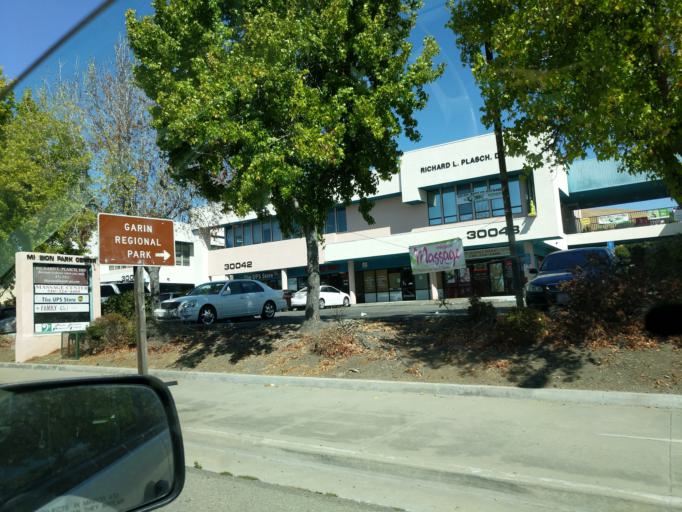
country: US
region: California
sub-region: Alameda County
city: Union City
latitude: 37.6266
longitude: -122.0431
